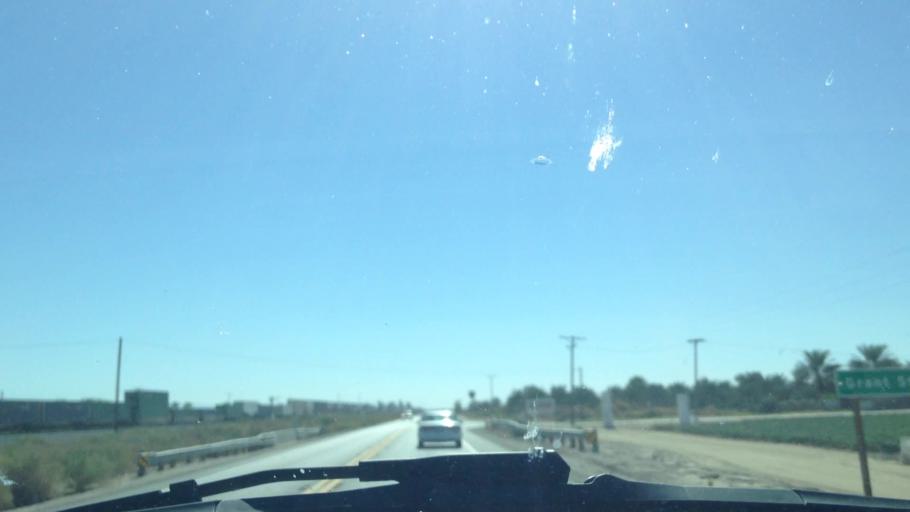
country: US
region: California
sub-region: Riverside County
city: Mecca
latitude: 33.5465
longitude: -116.0451
